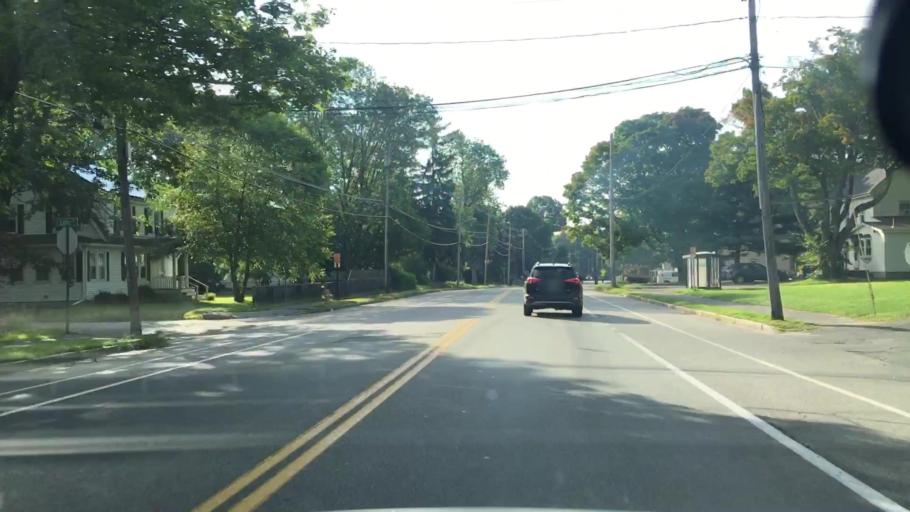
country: US
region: Maine
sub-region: Cumberland County
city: South Portland Gardens
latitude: 43.6954
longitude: -70.3043
